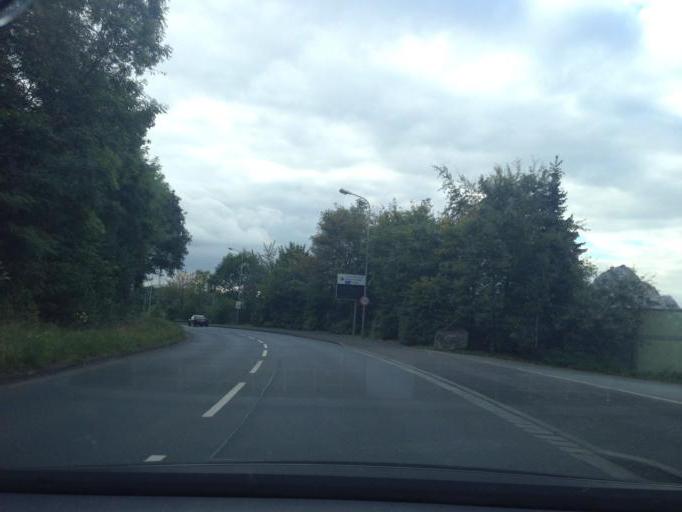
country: DE
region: Hesse
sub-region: Regierungsbezirk Giessen
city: Wetzlar
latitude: 50.5657
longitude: 8.5172
